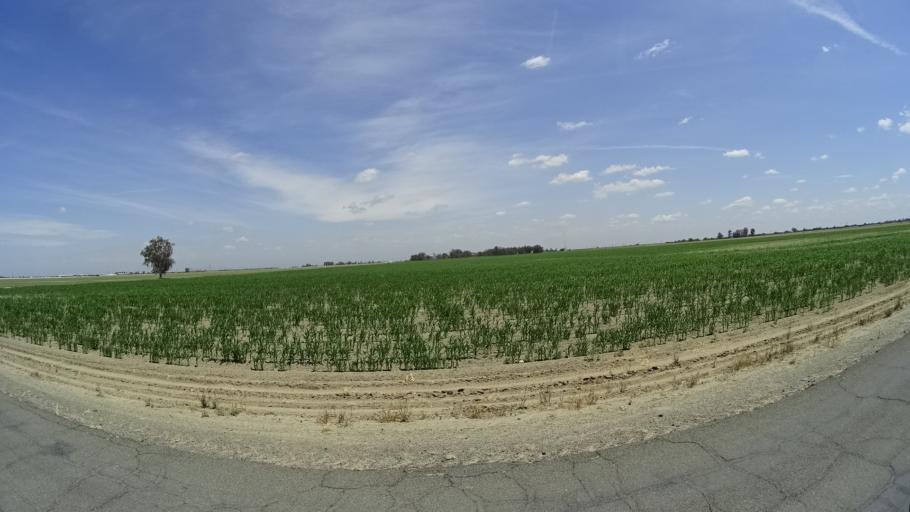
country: US
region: California
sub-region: Kings County
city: Home Garden
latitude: 36.2174
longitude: -119.6728
